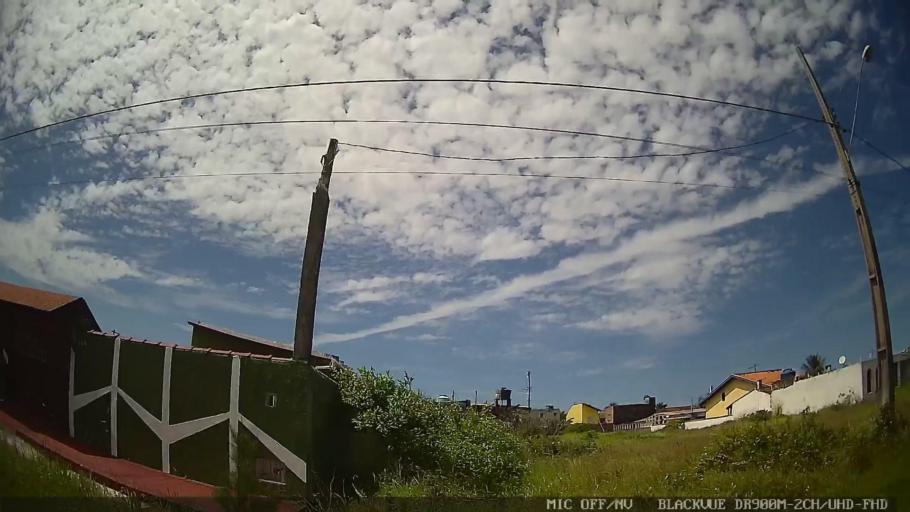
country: BR
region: Sao Paulo
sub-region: Iguape
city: Iguape
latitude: -24.7214
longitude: -47.5064
